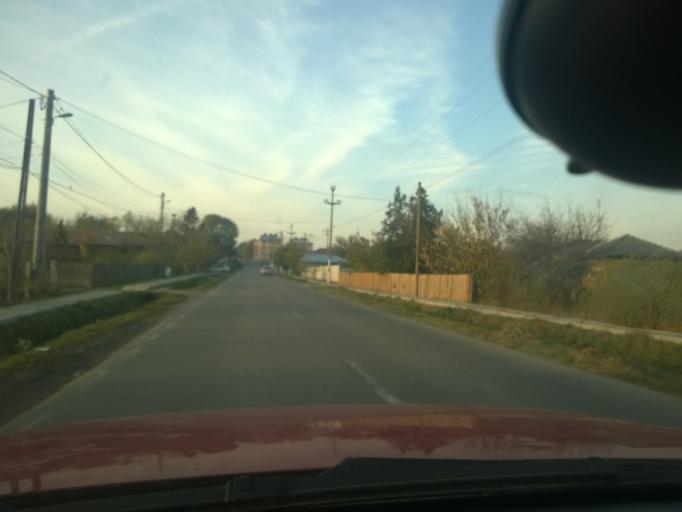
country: RO
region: Giurgiu
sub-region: Comuna Herasti
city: Herasti
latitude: 44.2071
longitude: 26.3591
